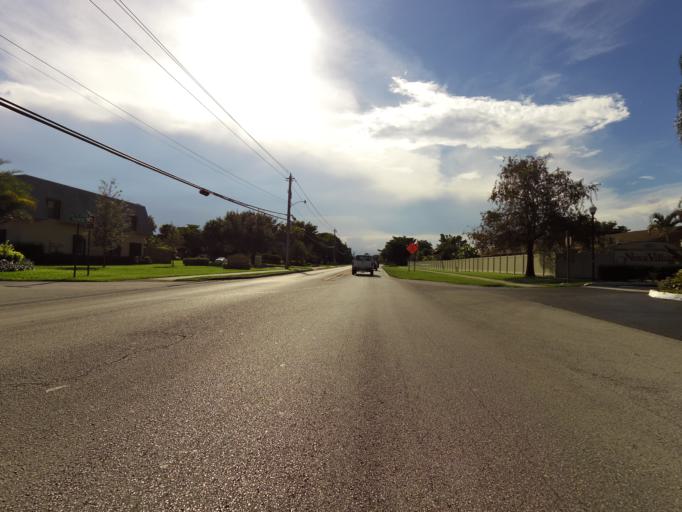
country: US
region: Florida
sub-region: Broward County
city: Pine Island Ridge
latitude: 26.0899
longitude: -80.2455
